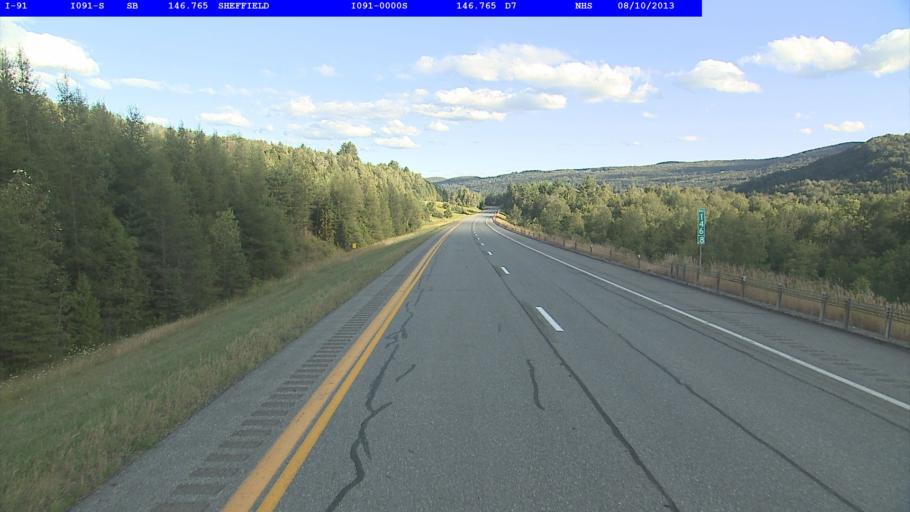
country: US
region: Vermont
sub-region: Caledonia County
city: Lyndonville
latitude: 44.6194
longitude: -72.1224
